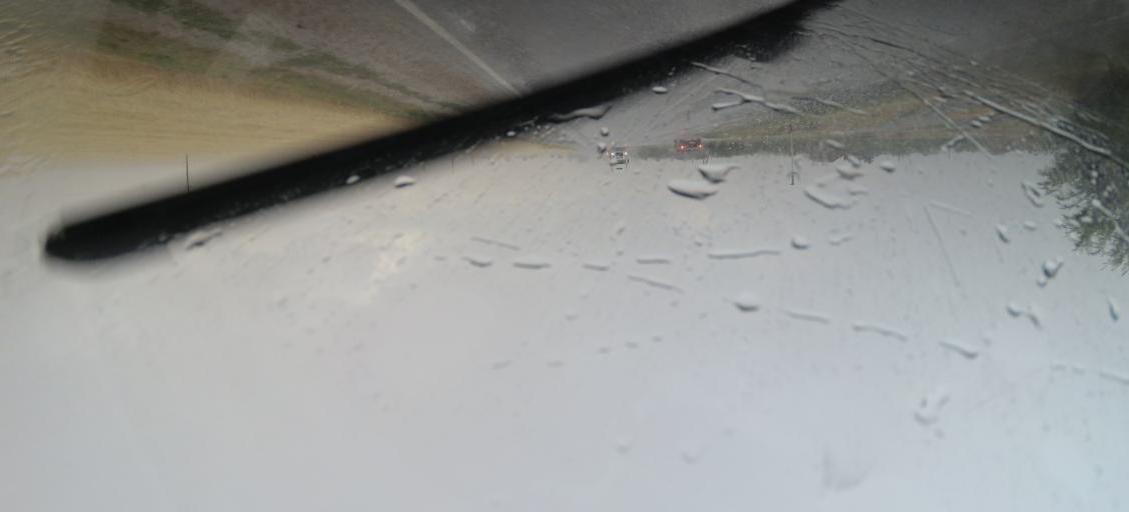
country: RU
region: Rostov
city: Proletarsk
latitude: 46.6819
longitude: 41.7155
